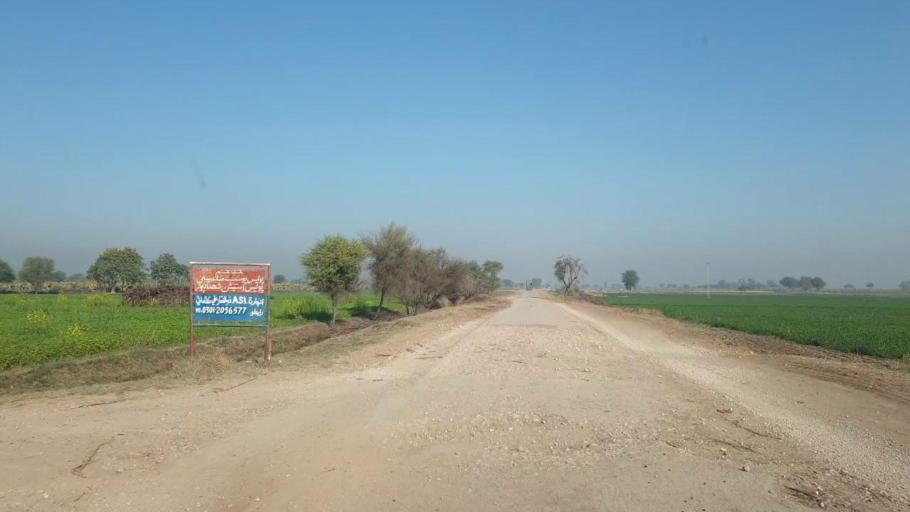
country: PK
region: Sindh
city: Shahdadpur
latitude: 25.9423
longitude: 68.5032
